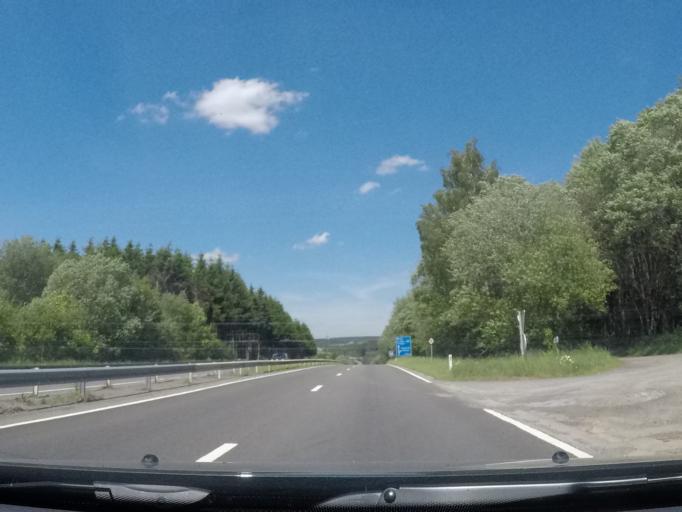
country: BE
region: Wallonia
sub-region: Province du Luxembourg
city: Saint-Hubert
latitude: 49.9985
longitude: 5.3815
